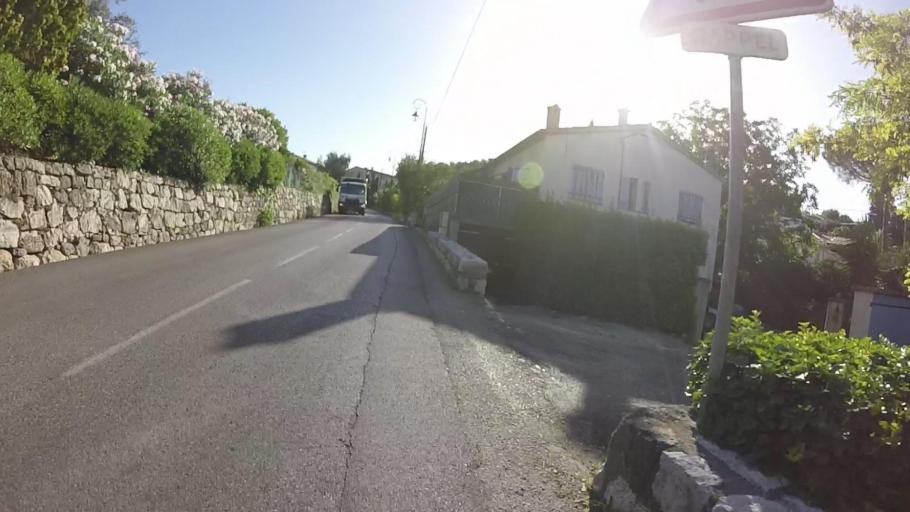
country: FR
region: Provence-Alpes-Cote d'Azur
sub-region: Departement des Alpes-Maritimes
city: Chateauneuf-Grasse
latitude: 43.6678
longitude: 6.9915
